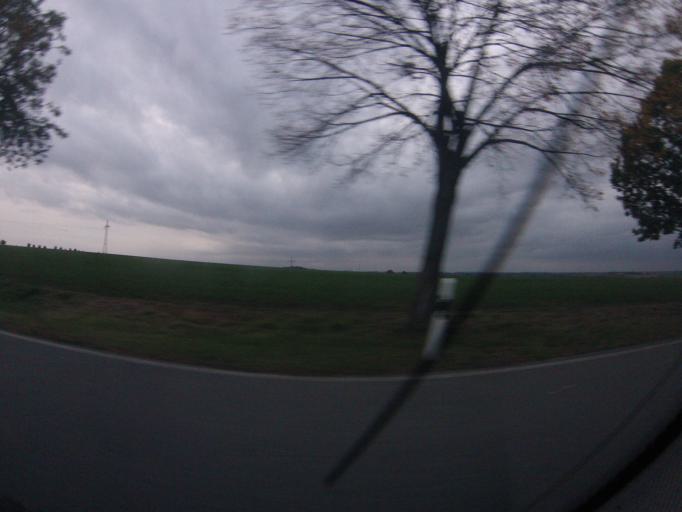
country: DE
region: Thuringia
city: Saara
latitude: 50.9108
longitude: 12.4020
